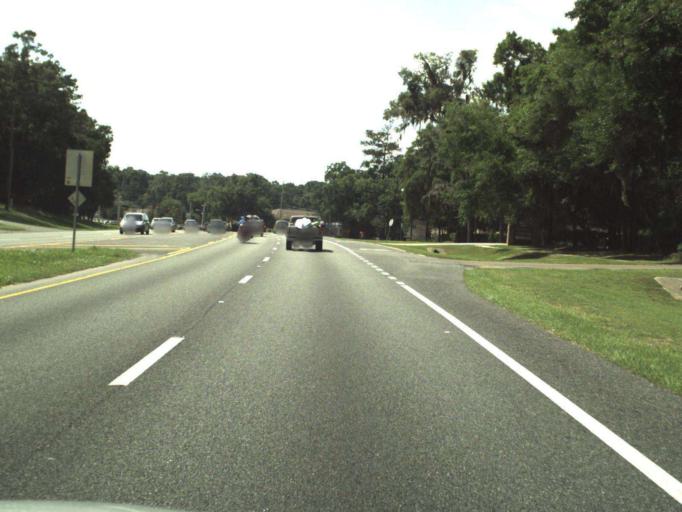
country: US
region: Florida
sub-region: Marion County
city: Ocala
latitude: 29.1695
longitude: -82.1003
